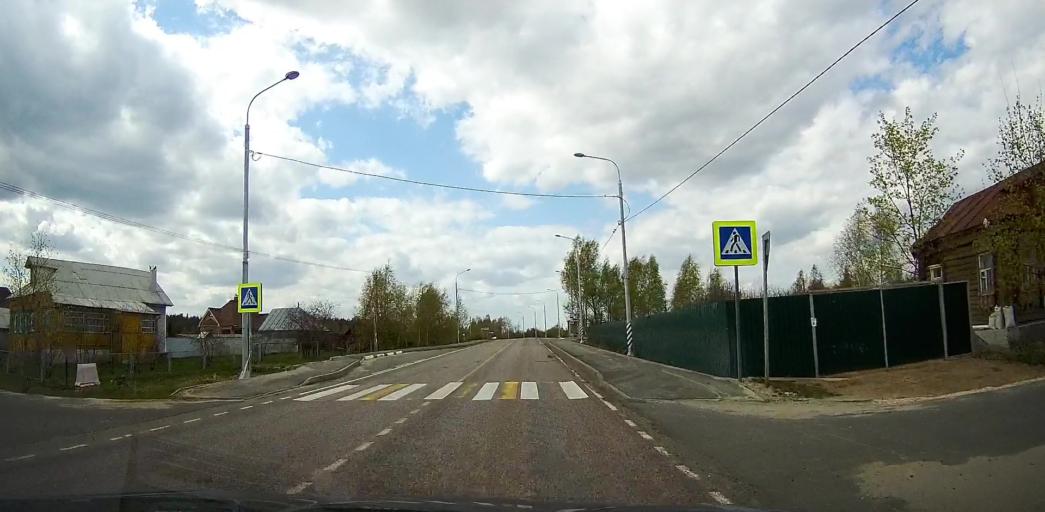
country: RU
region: Moskovskaya
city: Davydovo
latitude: 55.6648
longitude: 38.8003
